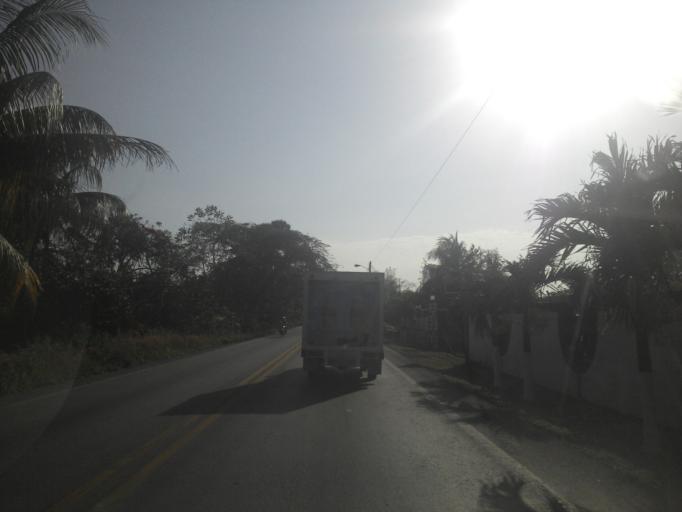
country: MX
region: Yucatan
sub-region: Valladolid
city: Tikuch
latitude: 20.7014
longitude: -88.1133
